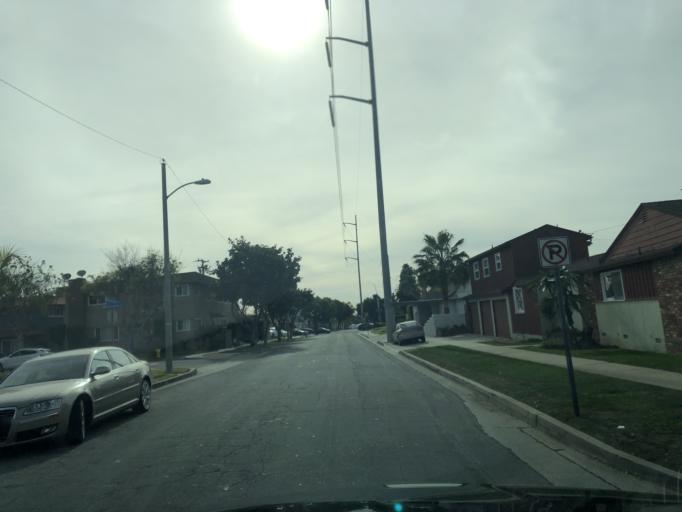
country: US
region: California
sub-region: Los Angeles County
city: Inglewood
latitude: 33.9776
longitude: -118.3598
